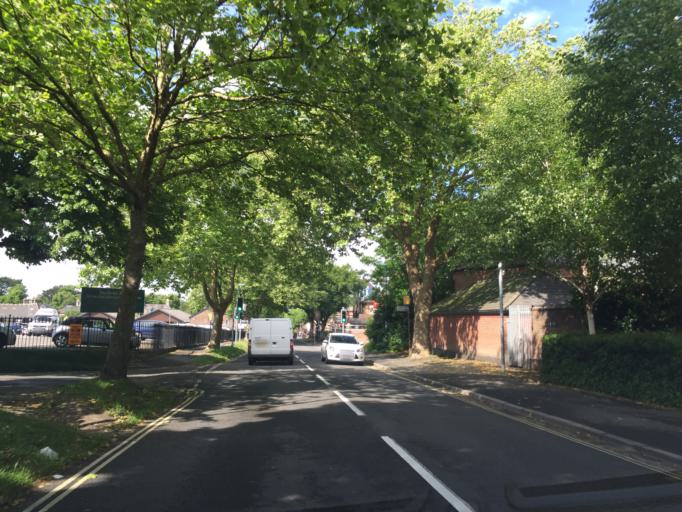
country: GB
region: England
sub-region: Dorset
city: Dorchester
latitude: 50.7091
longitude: -2.4402
